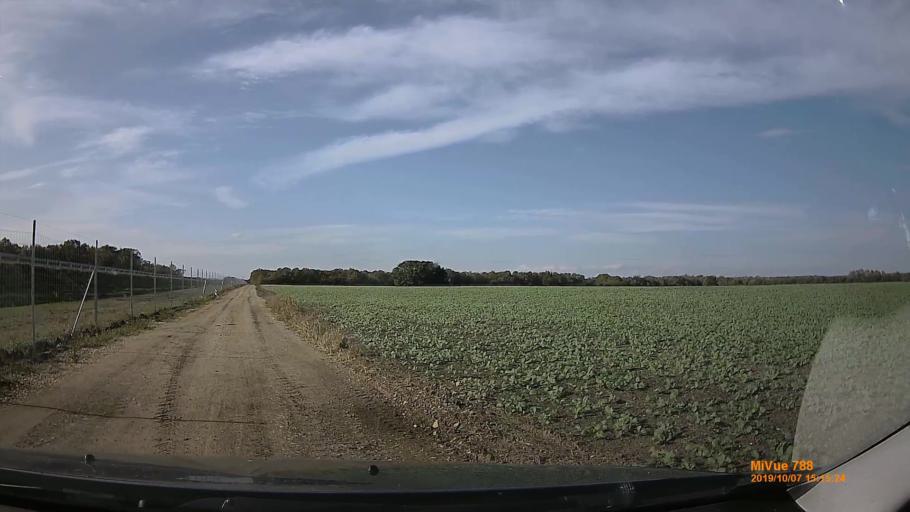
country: HU
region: Jasz-Nagykun-Szolnok
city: Kunszentmarton
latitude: 46.8545
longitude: 20.3148
